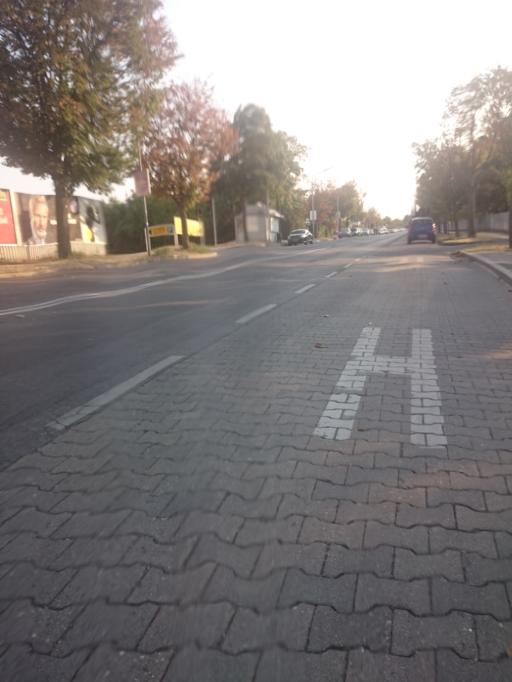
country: AT
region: Lower Austria
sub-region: Politischer Bezirk Wien-Umgebung
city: Gerasdorf bei Wien
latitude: 48.2669
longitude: 16.4280
